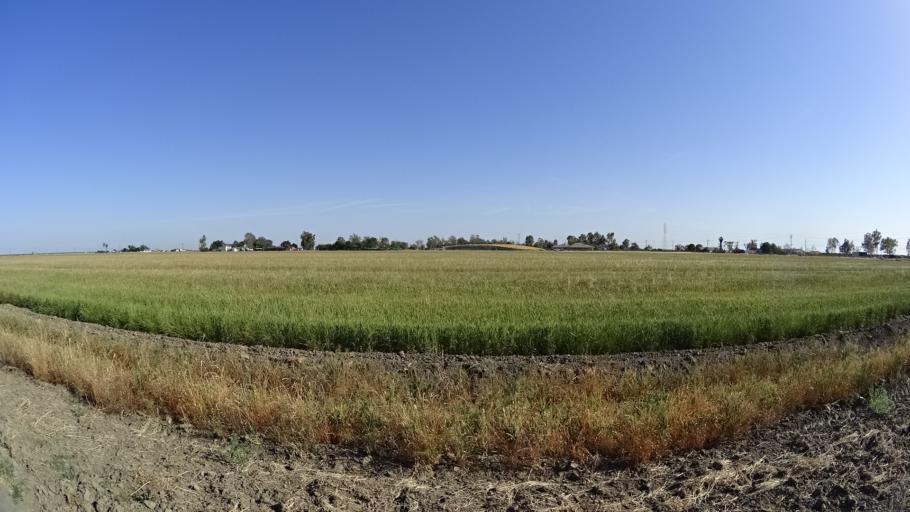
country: US
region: California
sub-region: Kings County
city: Corcoran
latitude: 36.1161
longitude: -119.5652
